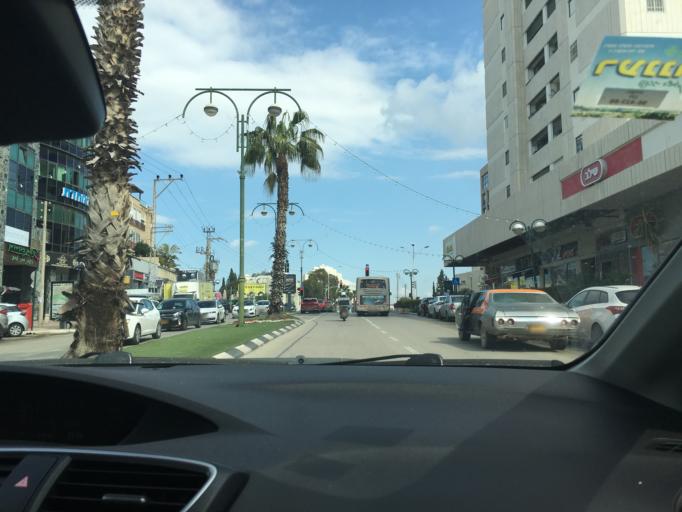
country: IL
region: Tel Aviv
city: Ramat HaSharon
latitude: 32.1481
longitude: 34.8395
